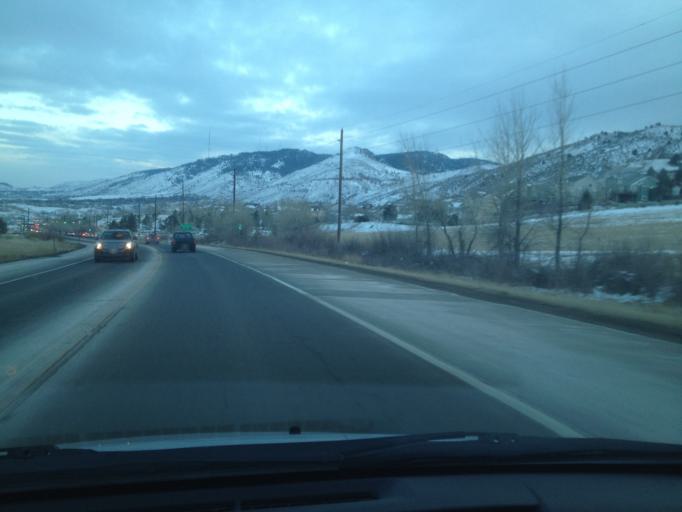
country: US
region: Colorado
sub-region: Jefferson County
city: Golden
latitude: 39.7707
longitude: -105.2365
